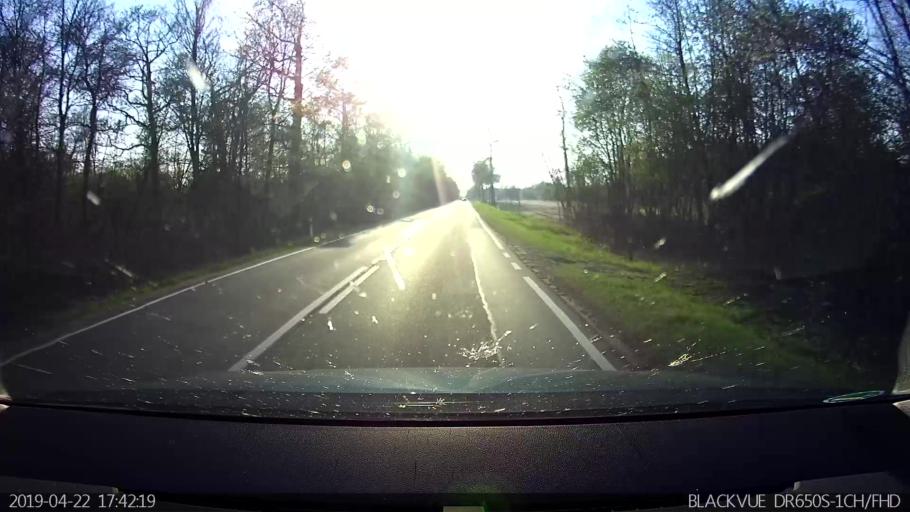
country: PL
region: Masovian Voivodeship
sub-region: Powiat wegrowski
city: Miedzna
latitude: 52.4040
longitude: 22.0823
